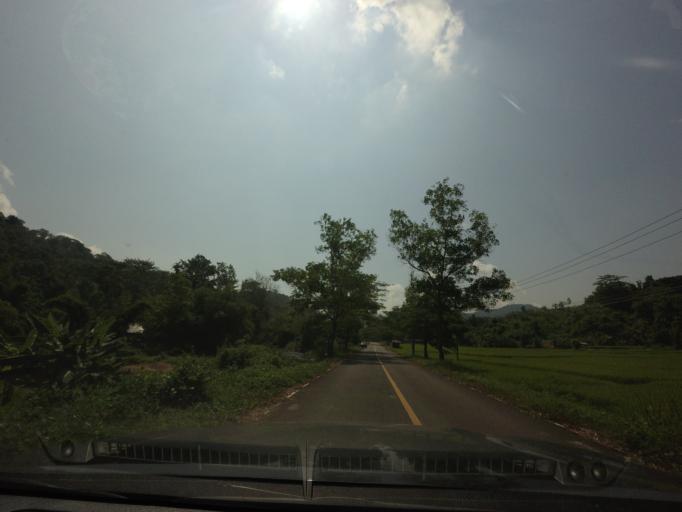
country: TH
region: Nan
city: Bo Kluea
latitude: 19.0404
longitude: 101.1713
